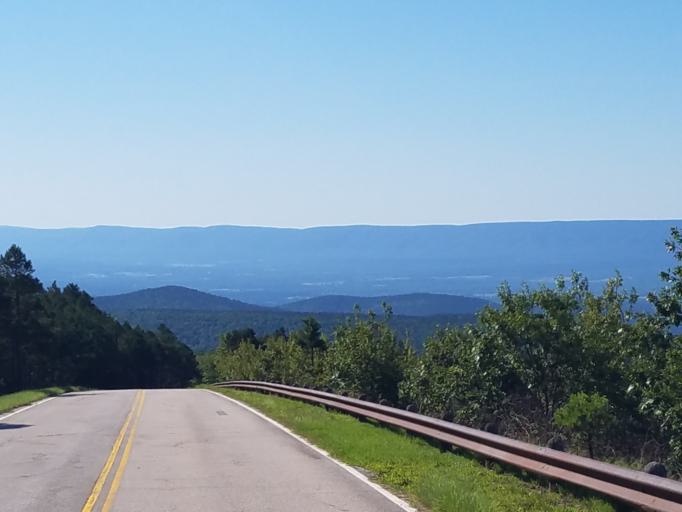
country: US
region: Oklahoma
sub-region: Le Flore County
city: Talihina
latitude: 34.7744
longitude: -94.8969
